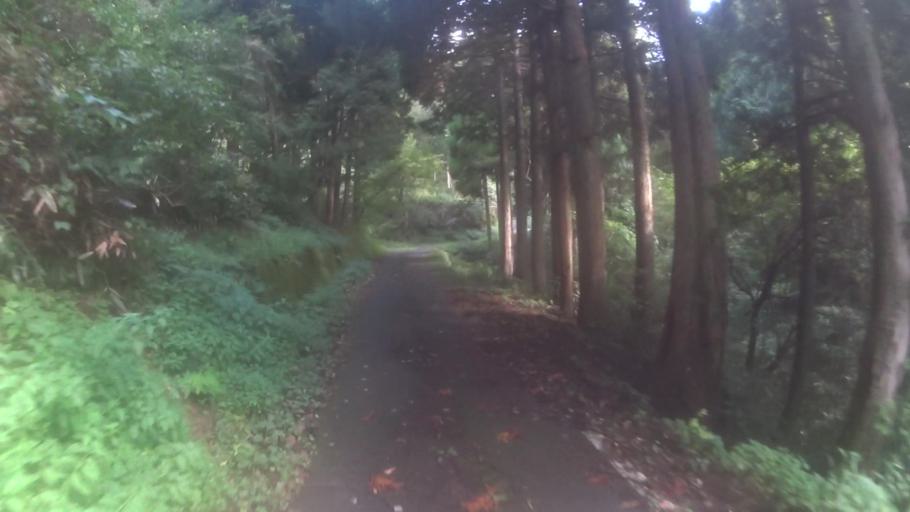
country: JP
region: Kyoto
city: Miyazu
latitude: 35.6218
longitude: 135.1552
